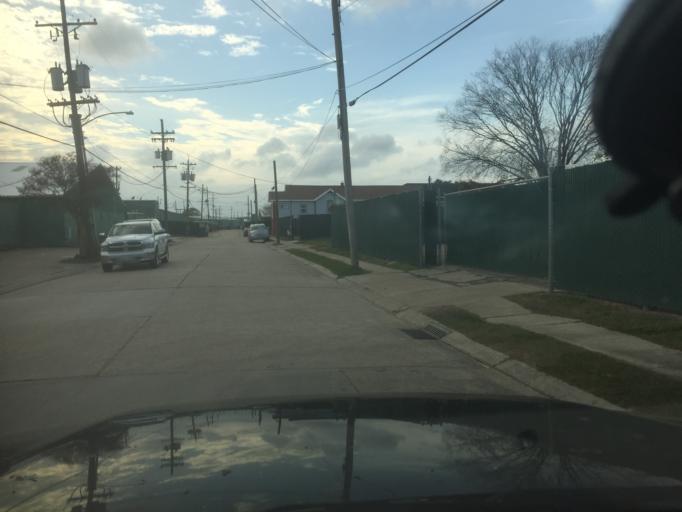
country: US
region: Louisiana
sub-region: Orleans Parish
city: New Orleans
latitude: 29.9860
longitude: -90.0813
